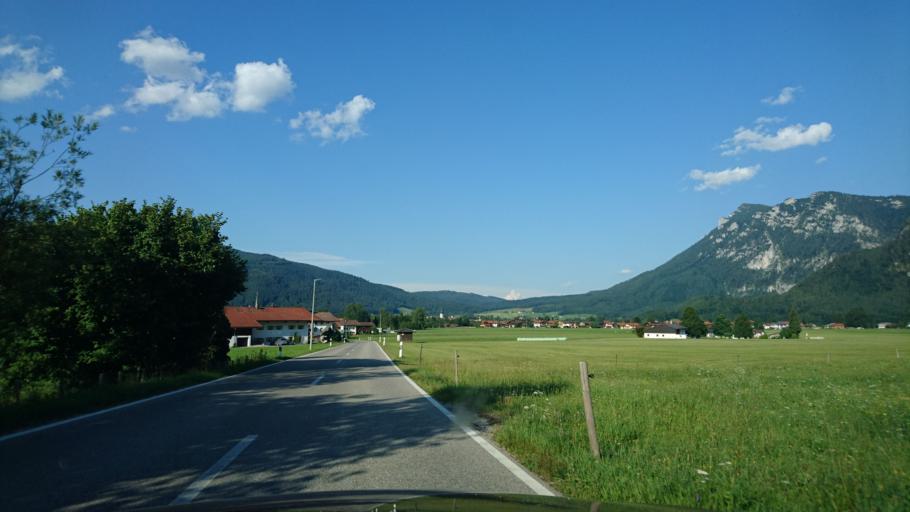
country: DE
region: Bavaria
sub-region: Upper Bavaria
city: Inzell
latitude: 47.7571
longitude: 12.7317
